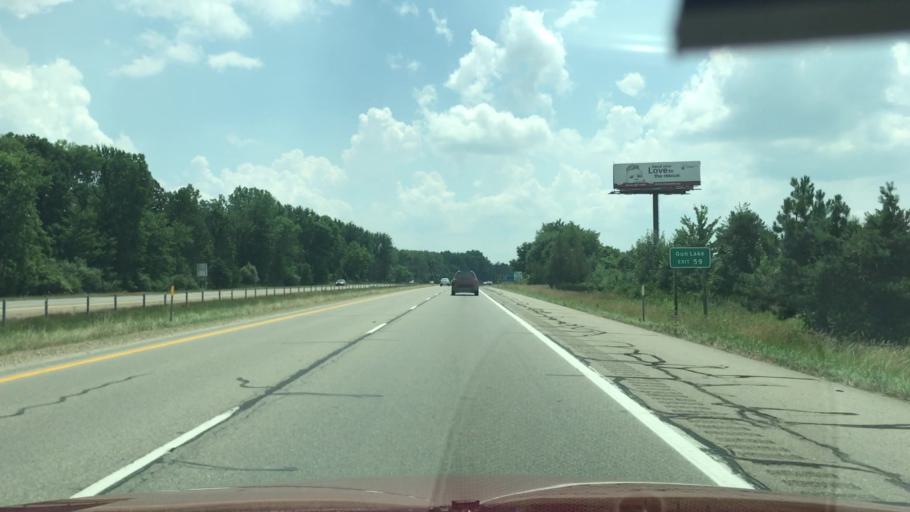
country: US
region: Michigan
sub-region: Allegan County
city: Wayland
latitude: 42.6106
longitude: -85.6607
